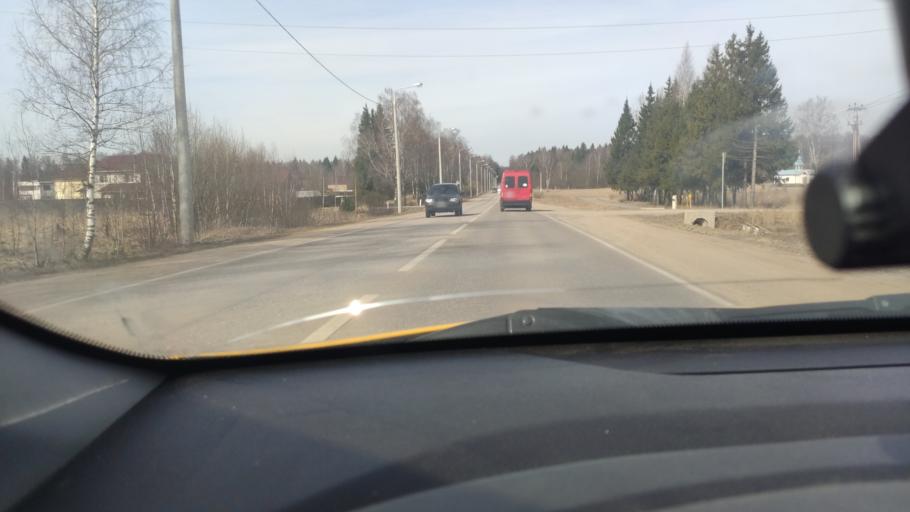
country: RU
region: Moskovskaya
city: Ruza
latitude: 55.7146
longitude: 36.1728
